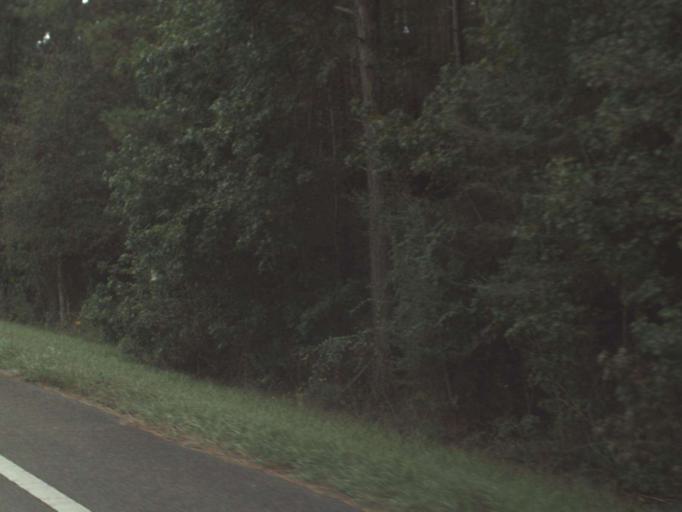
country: US
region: Florida
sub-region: Walton County
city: DeFuniak Springs
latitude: 30.6884
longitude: -85.9365
